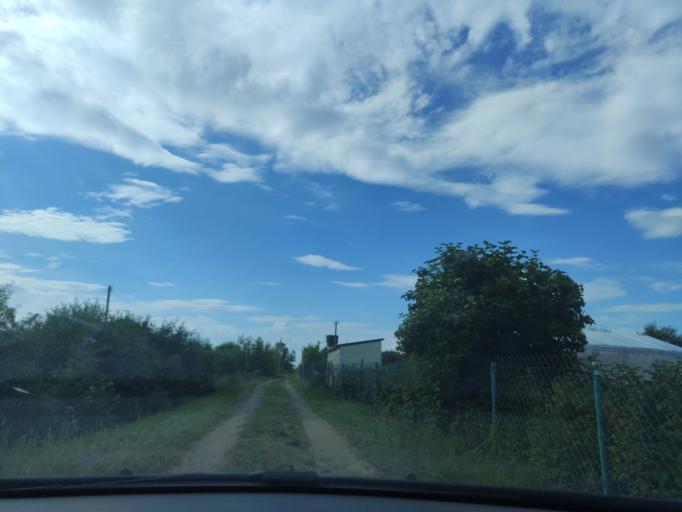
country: RU
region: Ulyanovsk
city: Cherdakly
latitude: 54.4424
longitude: 48.8967
